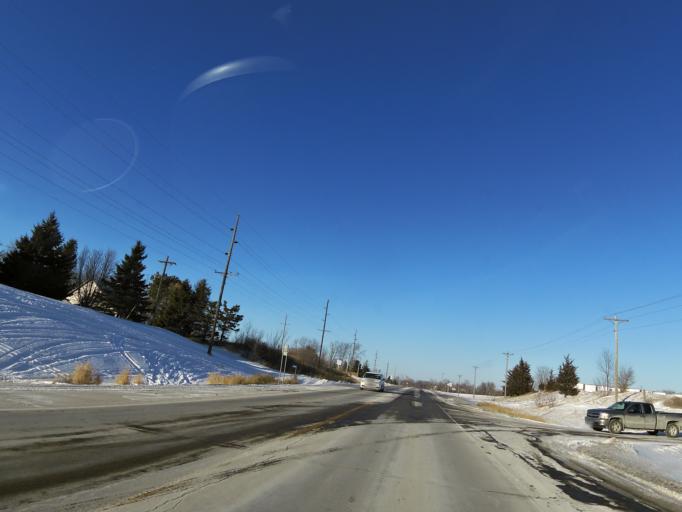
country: US
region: Minnesota
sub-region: Le Sueur County
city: New Prague
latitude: 44.5529
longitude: -93.5845
